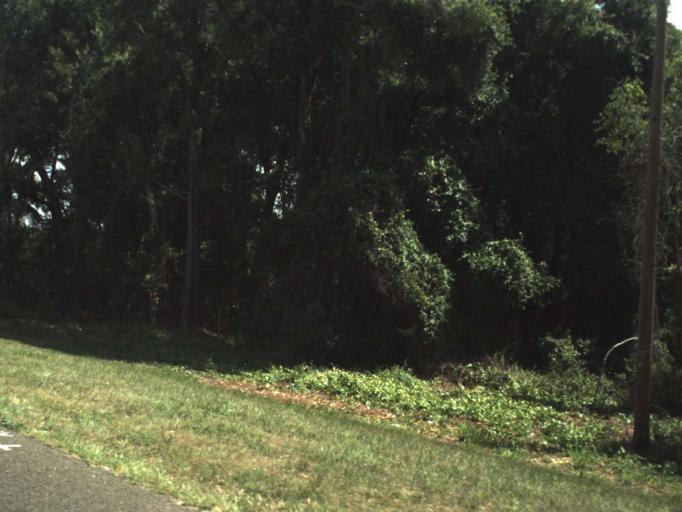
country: US
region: Florida
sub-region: Lake County
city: Mount Dora
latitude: 28.8106
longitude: -81.6257
